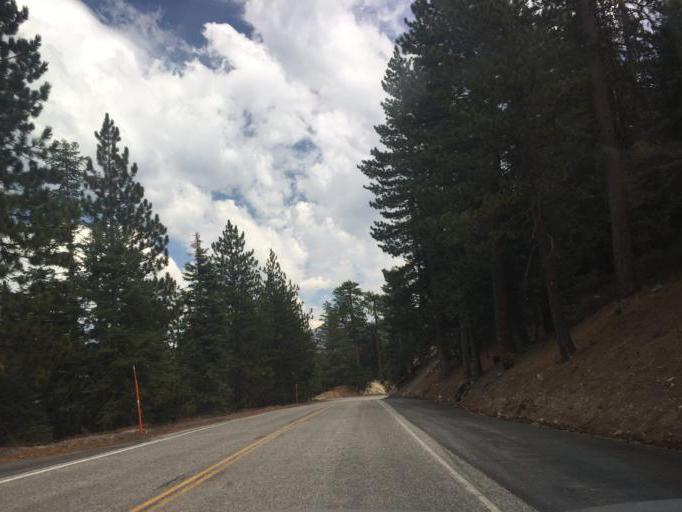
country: US
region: California
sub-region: Los Angeles County
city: Littlerock
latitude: 34.3528
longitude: -117.8881
